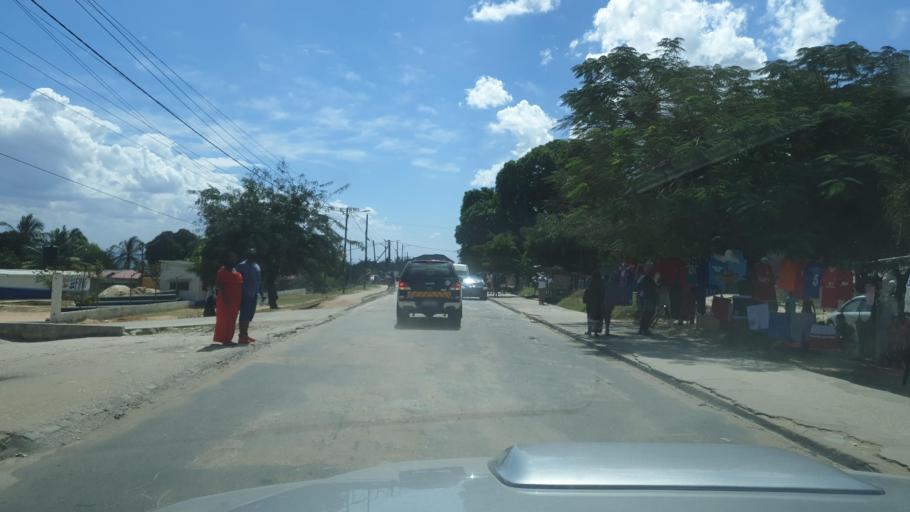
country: MZ
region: Nampula
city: Nacala
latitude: -14.5530
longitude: 40.6852
